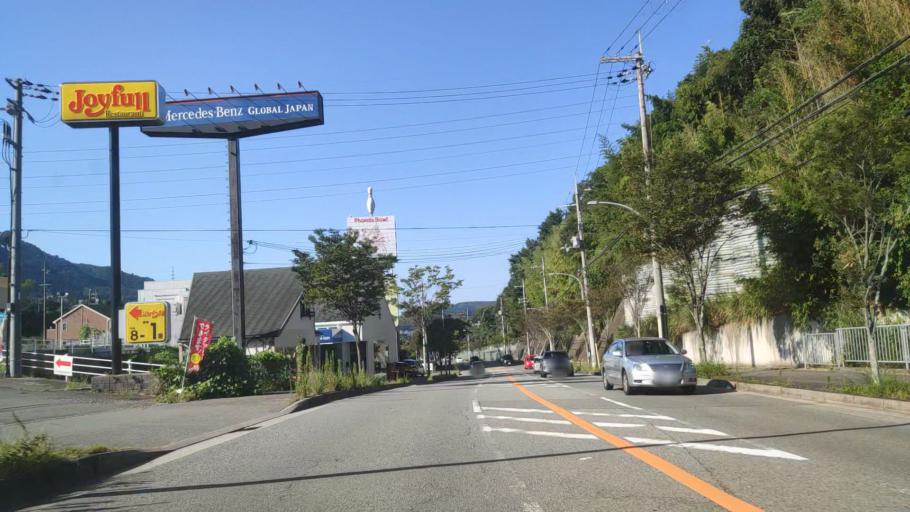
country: JP
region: Hyogo
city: Kobe
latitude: 34.7735
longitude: 135.1934
